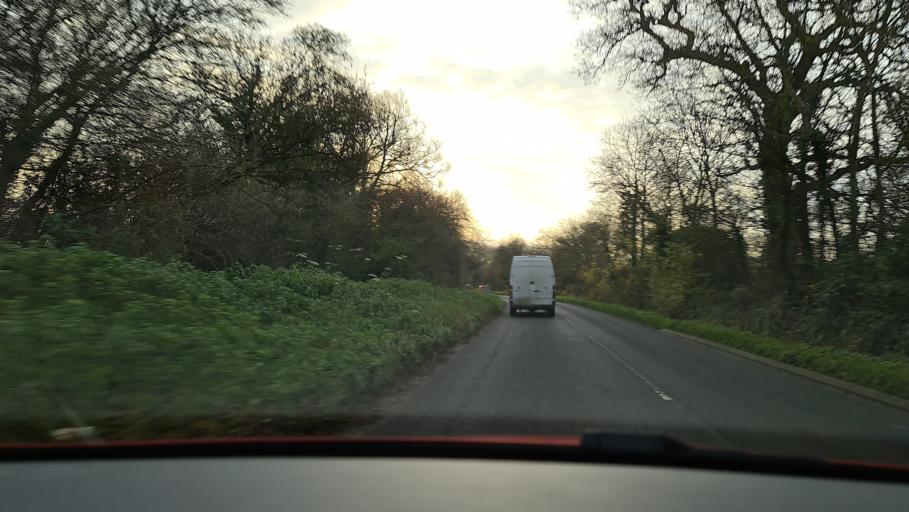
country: GB
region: England
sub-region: Oxfordshire
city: Kidlington
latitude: 51.8469
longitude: -1.2526
